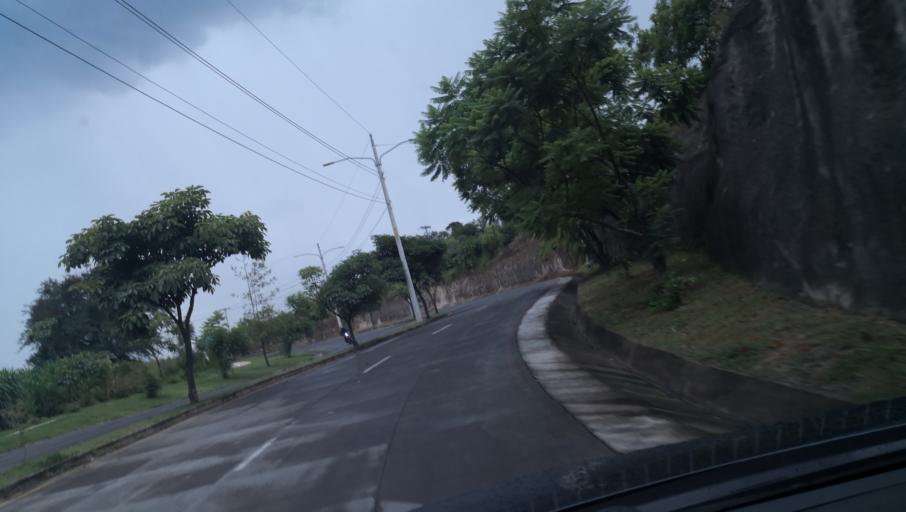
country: GT
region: Guatemala
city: Villa Nueva
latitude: 14.5569
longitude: -90.5950
